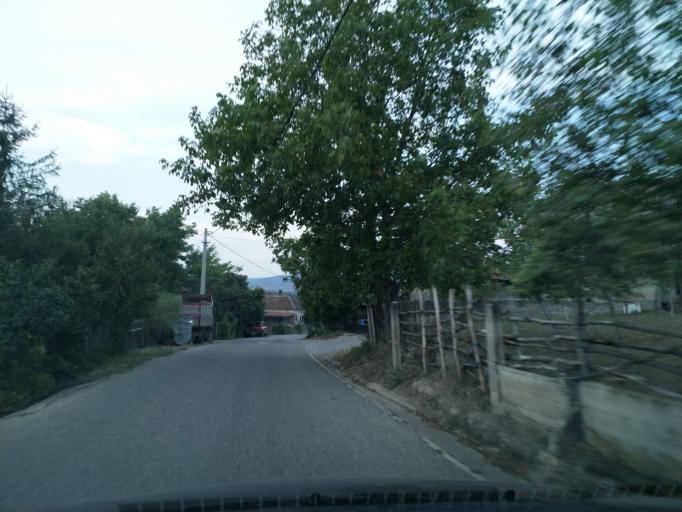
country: RS
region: Central Serbia
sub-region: Pomoravski Okrug
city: Paracin
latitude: 43.8503
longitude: 21.5280
